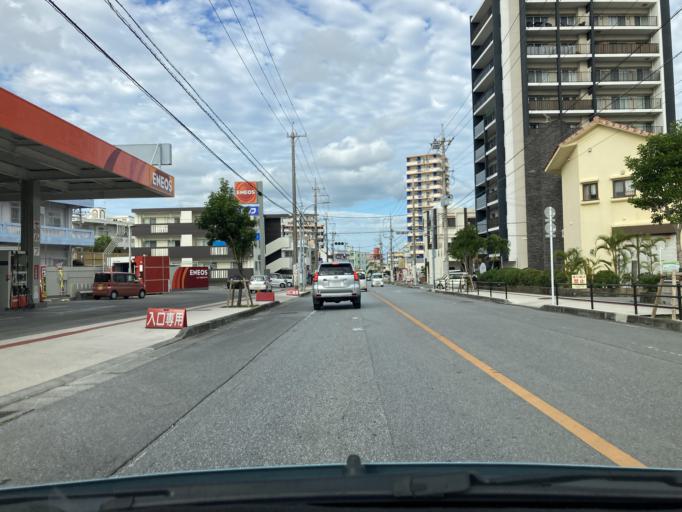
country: JP
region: Okinawa
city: Okinawa
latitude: 26.3397
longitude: 127.8217
